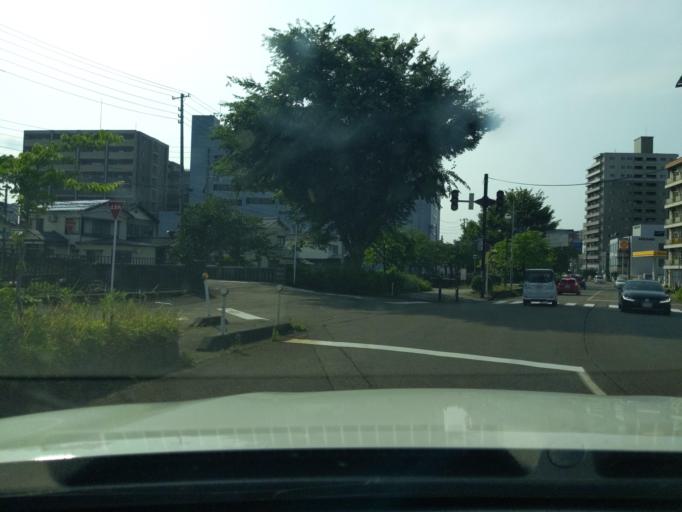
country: JP
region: Niigata
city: Nagaoka
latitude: 37.4434
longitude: 138.8501
